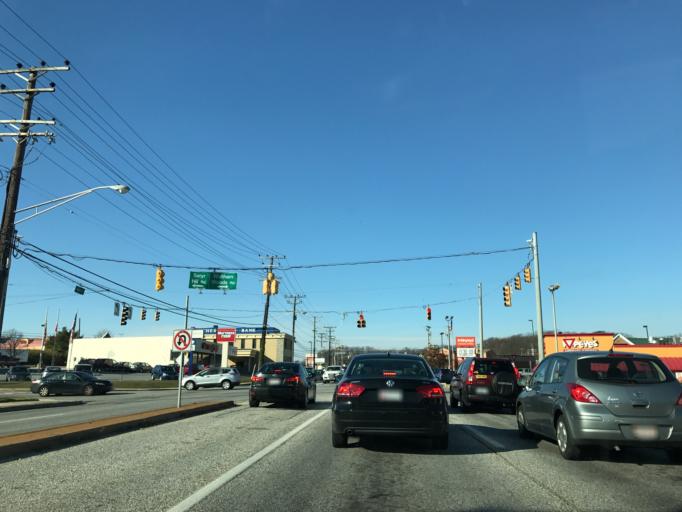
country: US
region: Maryland
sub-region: Baltimore County
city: Carney
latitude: 39.3985
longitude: -76.5421
